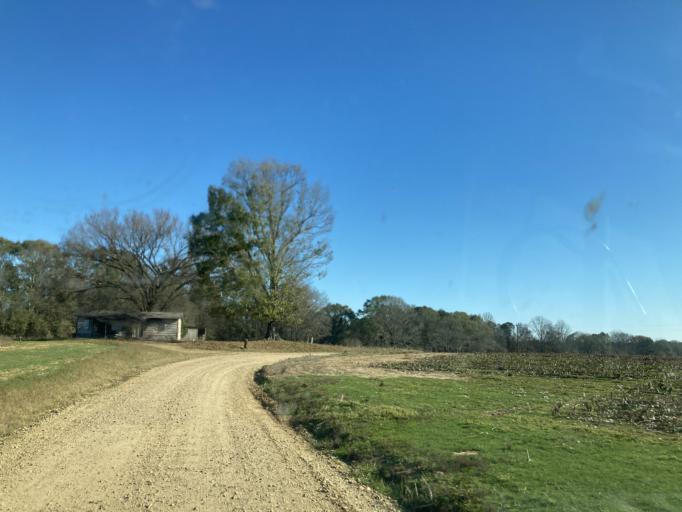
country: US
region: Mississippi
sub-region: Madison County
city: Kearney Park
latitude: 32.7259
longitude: -90.3079
